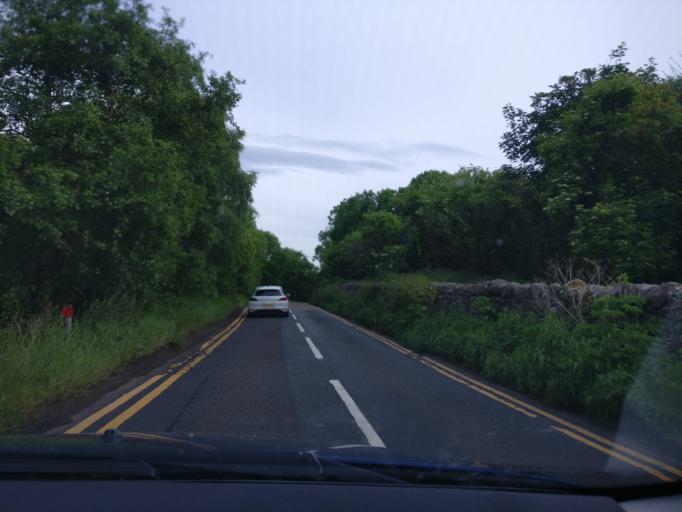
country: GB
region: Scotland
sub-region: West Lothian
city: Seafield
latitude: 55.9251
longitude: -3.1379
